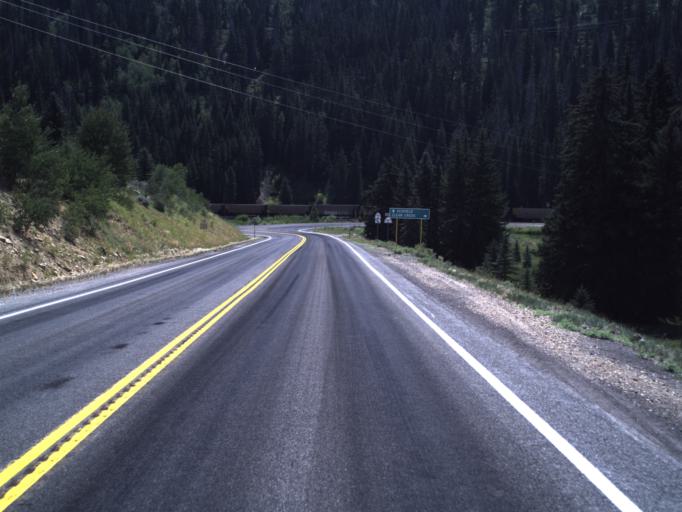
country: US
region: Utah
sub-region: Sanpete County
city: Fairview
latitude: 39.6856
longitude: -111.1585
